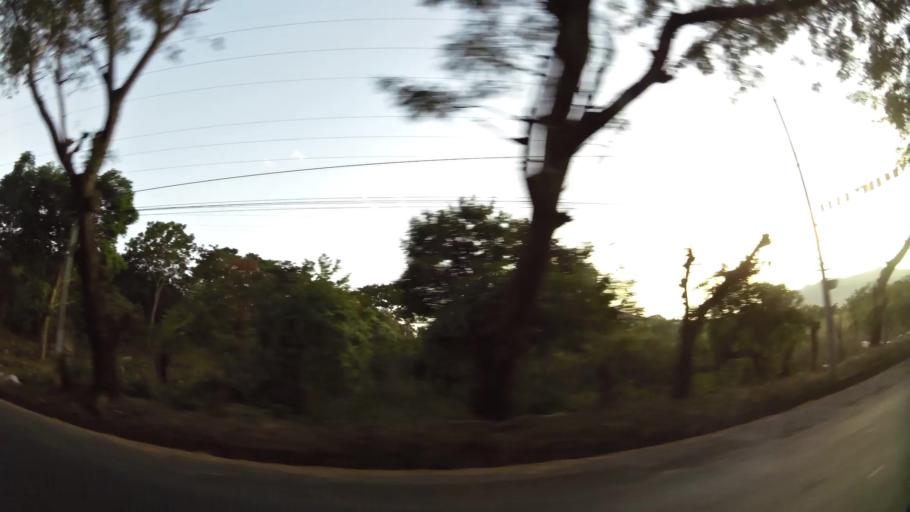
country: SV
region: San Miguel
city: Moncagua
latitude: 13.5037
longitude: -88.2243
